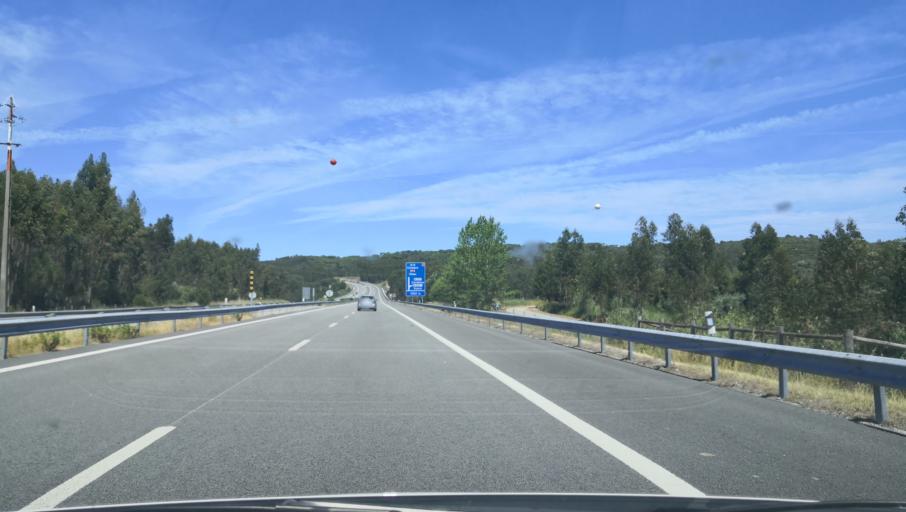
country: PT
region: Coimbra
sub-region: Montemor-O-Velho
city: Montemor-o-Velho
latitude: 40.1924
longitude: -8.6928
